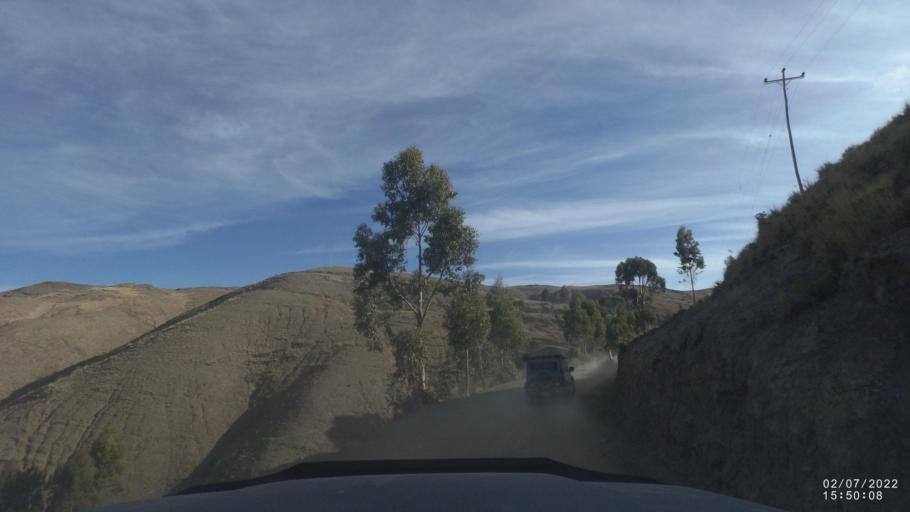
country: BO
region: Cochabamba
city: Irpa Irpa
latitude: -17.9032
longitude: -66.4120
